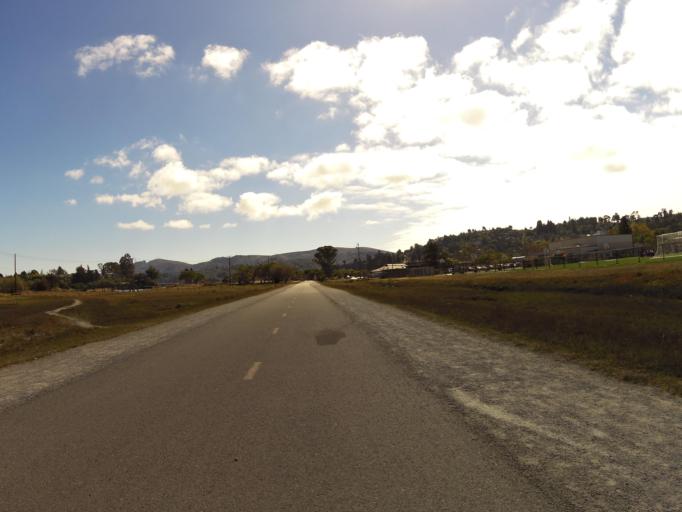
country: US
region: California
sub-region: Marin County
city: Strawberry
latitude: 37.8990
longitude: -122.5266
